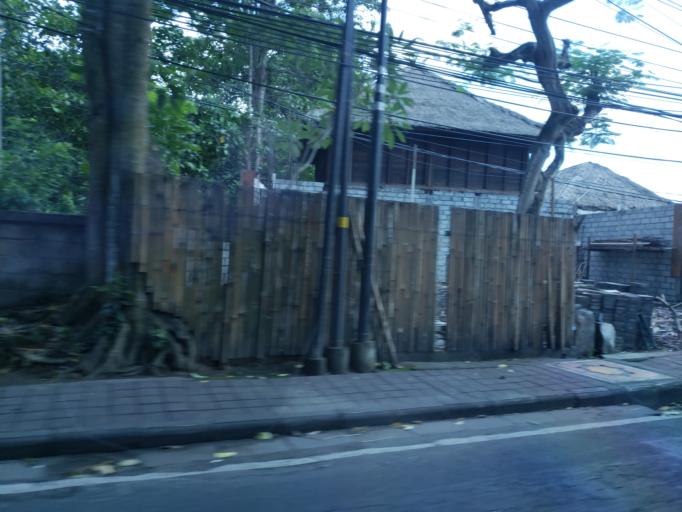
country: ID
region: Bali
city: Jimbaran
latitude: -8.7812
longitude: 115.1675
